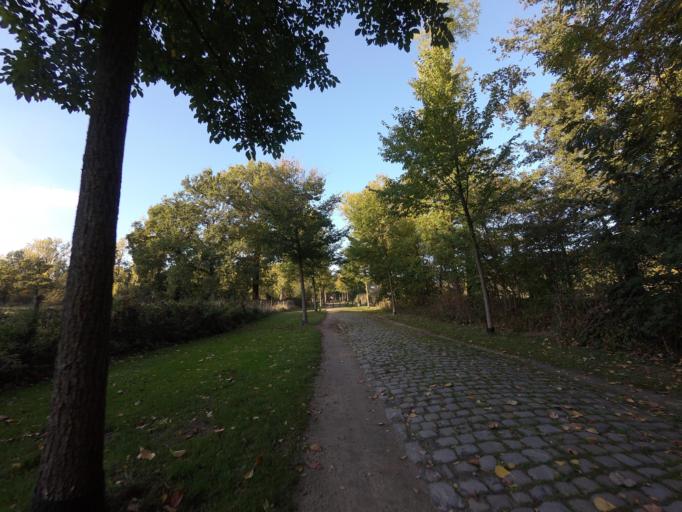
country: BE
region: Flanders
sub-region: Provincie Antwerpen
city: Stabroek
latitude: 51.3370
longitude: 4.3137
